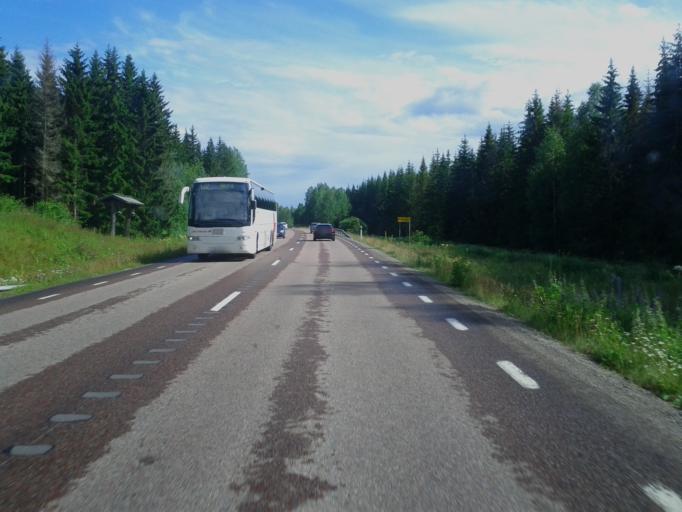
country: SE
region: Dalarna
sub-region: Faluns Kommun
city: Falun
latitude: 60.6532
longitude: 15.5575
